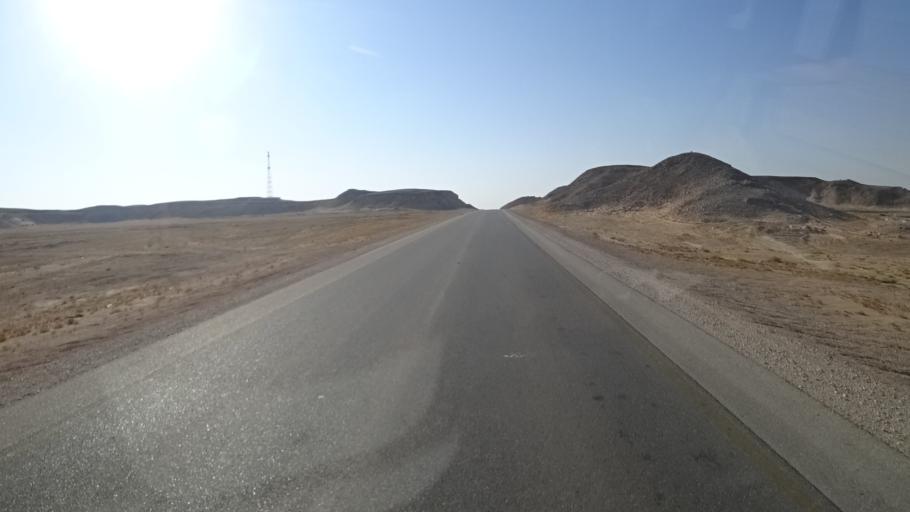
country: OM
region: Zufar
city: Salalah
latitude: 17.6417
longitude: 53.8581
